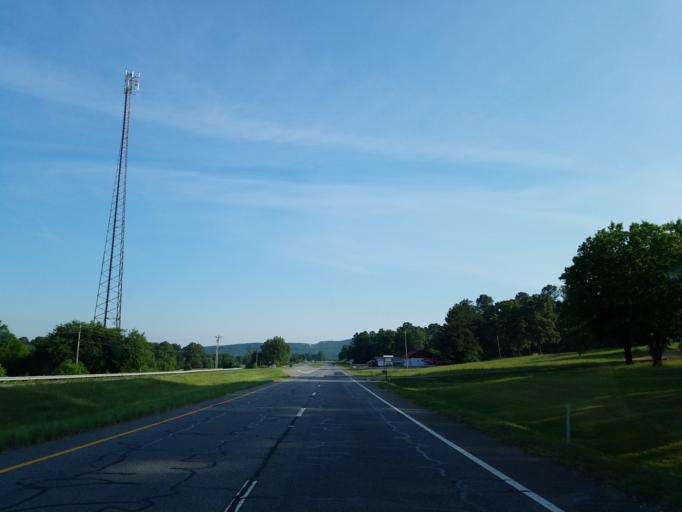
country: US
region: Georgia
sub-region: Chattooga County
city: Summerville
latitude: 34.4425
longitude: -85.2479
